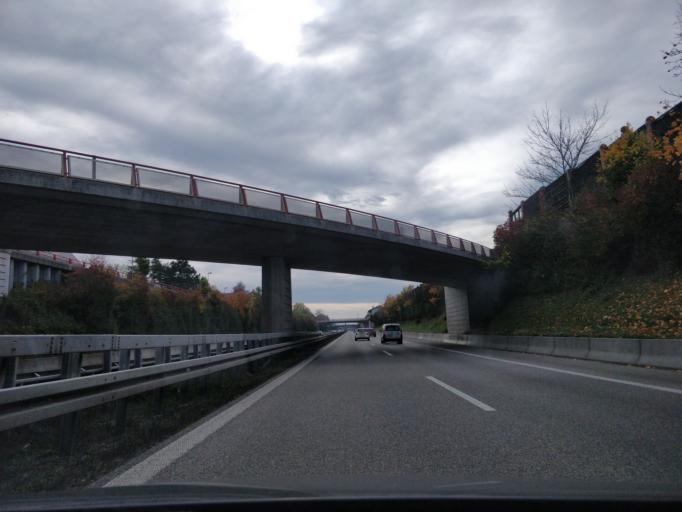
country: DE
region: Bavaria
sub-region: Swabia
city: Klosterlechfeld
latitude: 48.1859
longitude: 10.8461
